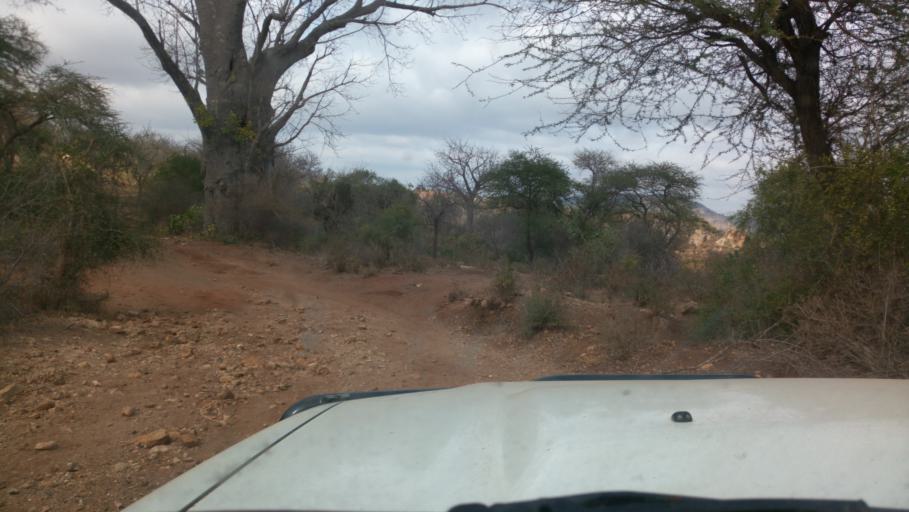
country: KE
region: Kitui
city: Kitui
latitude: -1.8620
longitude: 38.2878
